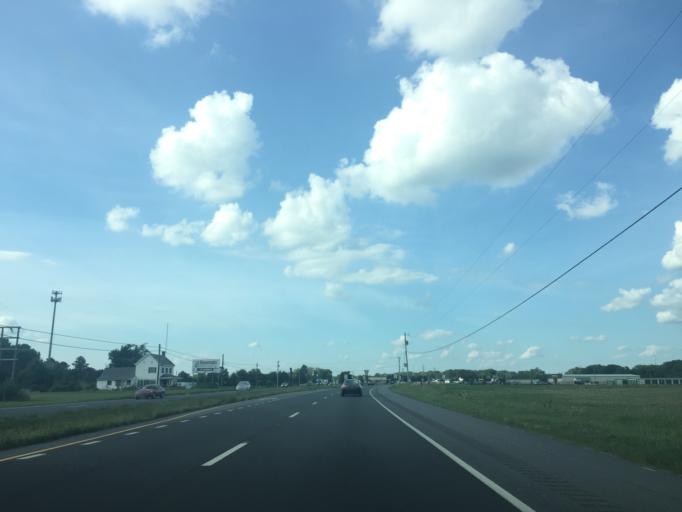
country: US
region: Delaware
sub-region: Sussex County
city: Bridgeville
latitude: 38.7981
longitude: -75.5879
